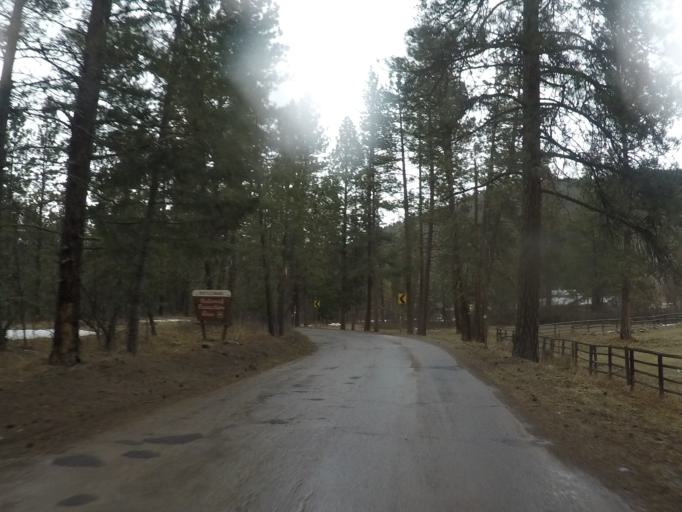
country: US
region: Montana
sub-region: Missoula County
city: East Missoula
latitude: 46.9177
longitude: -113.9602
